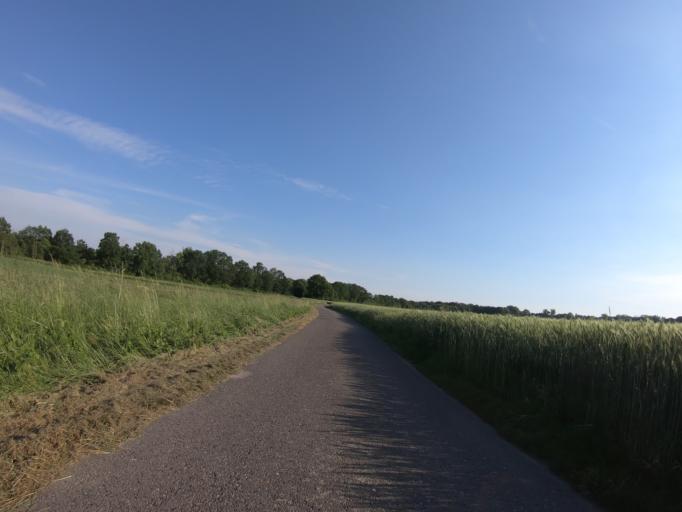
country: DE
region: Lower Saxony
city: Meine
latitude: 52.3608
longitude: 10.5532
